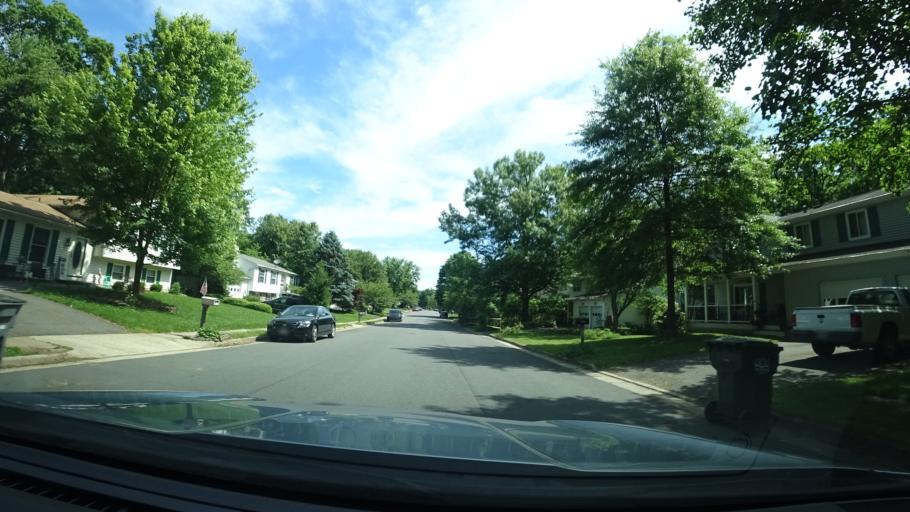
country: US
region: Virginia
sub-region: Loudoun County
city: Oak Grove
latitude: 38.9864
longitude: -77.3995
